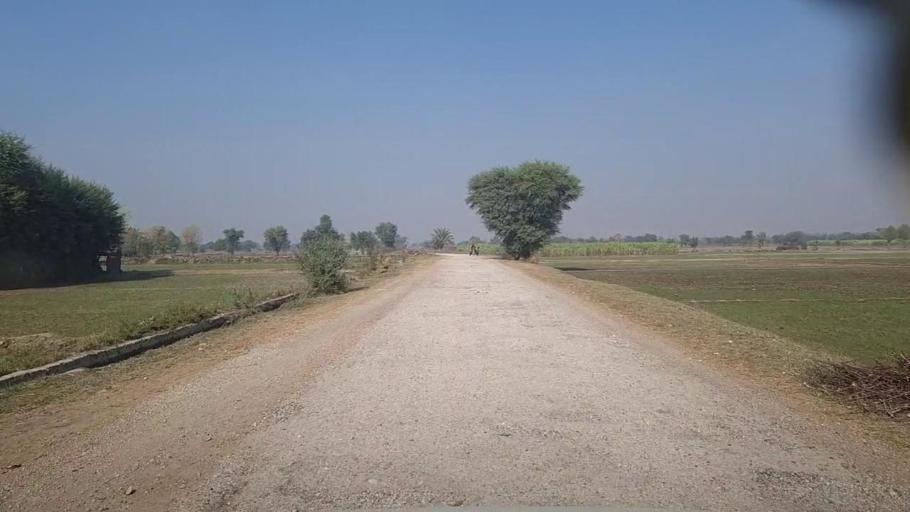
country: PK
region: Sindh
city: Kandiari
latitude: 26.9277
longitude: 68.5241
